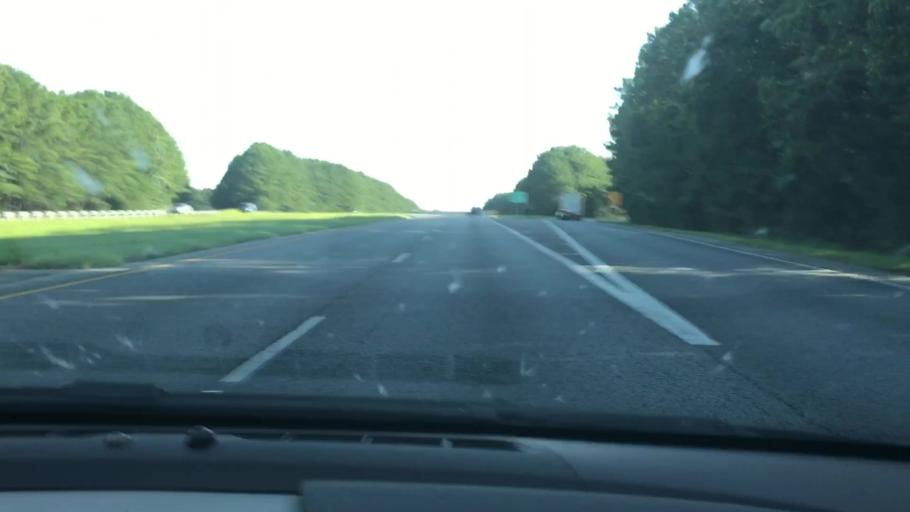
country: US
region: Alabama
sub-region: Russell County
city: Phenix City
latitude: 32.5722
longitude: -84.9621
